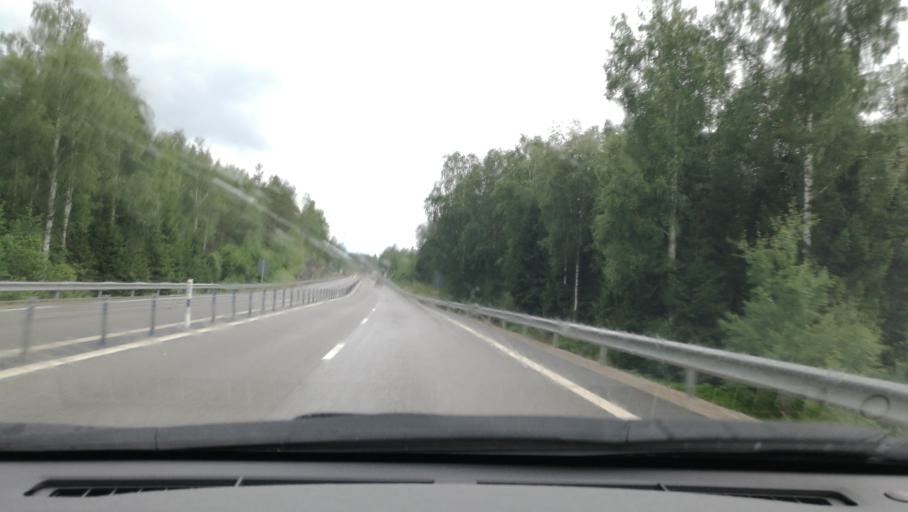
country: SE
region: OEstergoetland
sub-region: Norrkopings Kommun
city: Jursla
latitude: 58.8051
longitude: 16.1519
